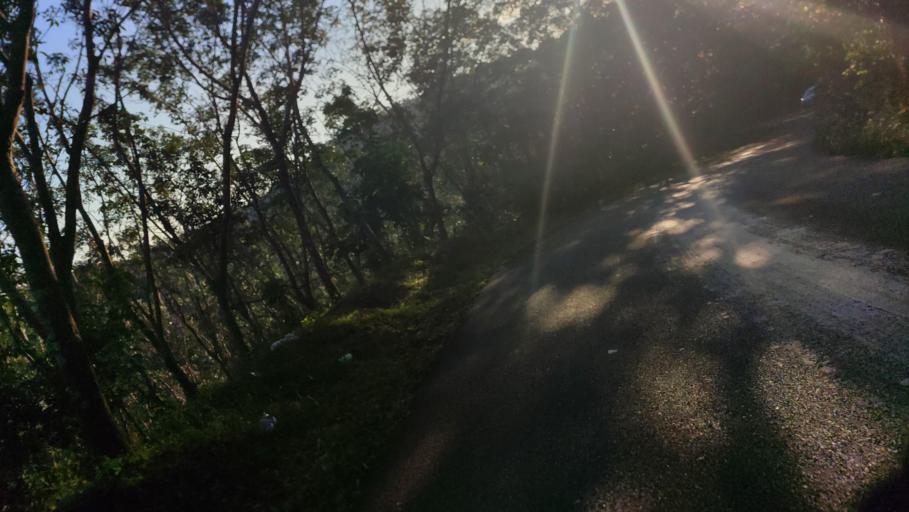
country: IN
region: Kerala
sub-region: Kasaragod District
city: Kasaragod
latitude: 12.4411
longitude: 75.0966
